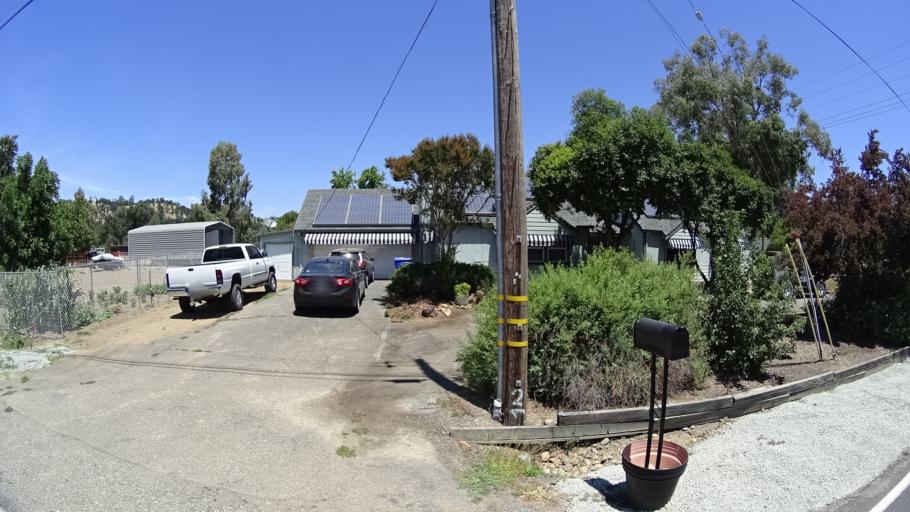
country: US
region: California
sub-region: Calaveras County
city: Rancho Calaveras
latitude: 38.1411
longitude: -120.8647
